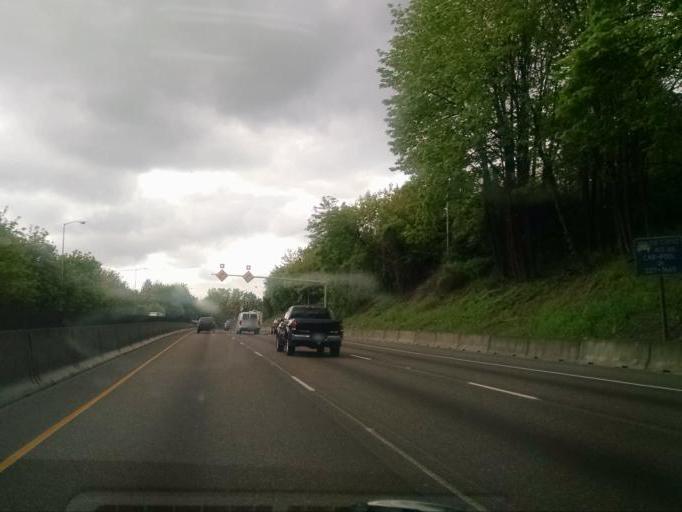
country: US
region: Oregon
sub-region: Clackamas County
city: Milwaukie
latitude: 45.4742
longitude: -122.6782
